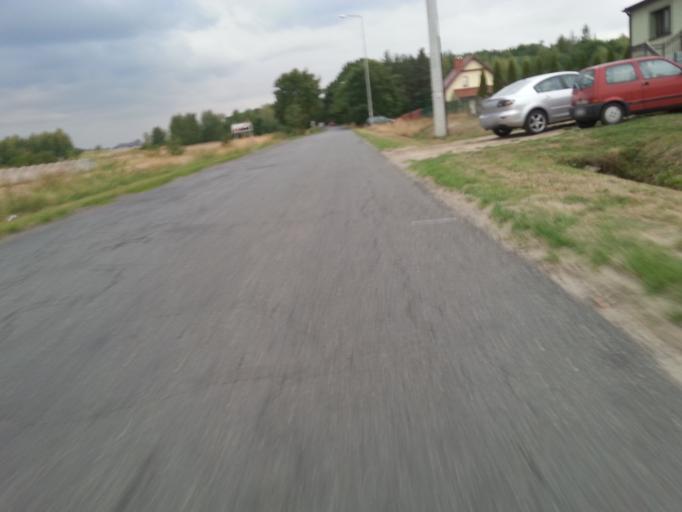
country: PL
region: Lower Silesian Voivodeship
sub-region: Powiat olesnicki
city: Twardogora
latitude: 51.3521
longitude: 17.4528
